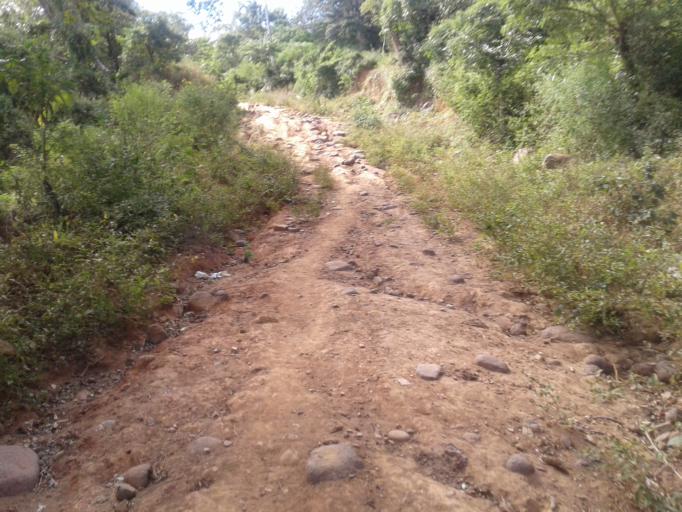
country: NI
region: Carazo
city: Santa Teresa
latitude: 11.6232
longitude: -86.1856
